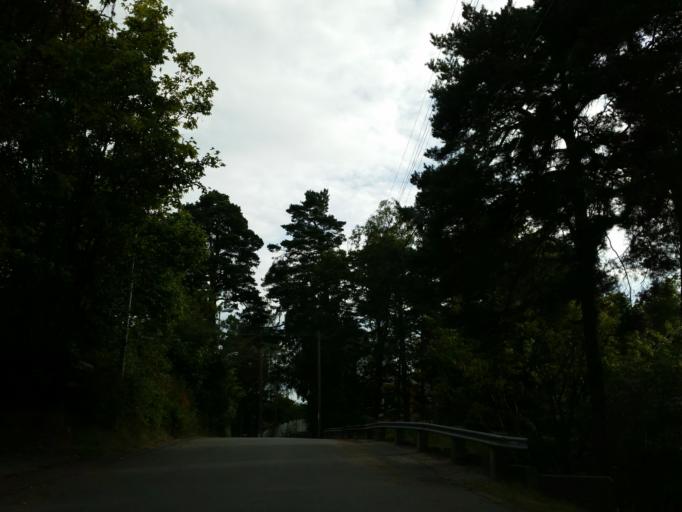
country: SE
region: Stockholm
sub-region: Sollentuna Kommun
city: Sollentuna
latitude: 59.4620
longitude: 17.9258
